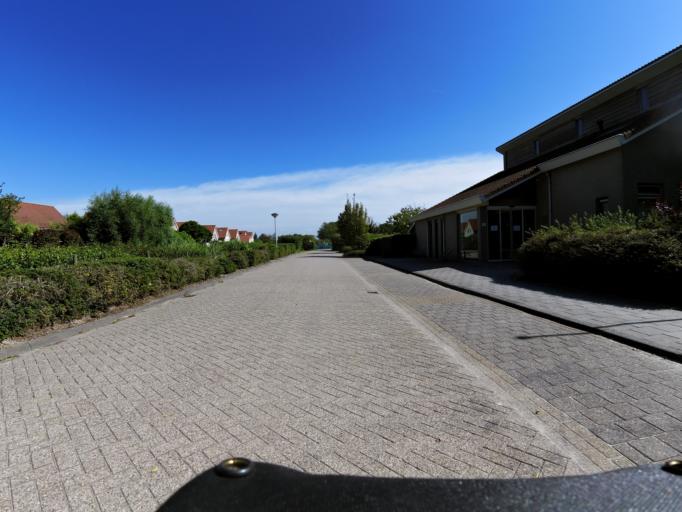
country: NL
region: South Holland
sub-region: Gemeente Goeree-Overflakkee
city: Goedereede
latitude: 51.8001
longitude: 4.0217
